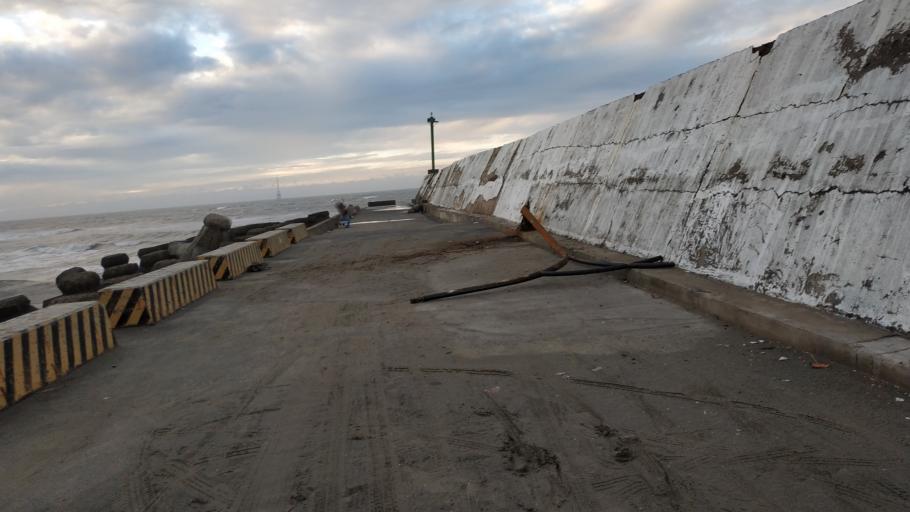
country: TW
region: Taiwan
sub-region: Miaoli
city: Miaoli
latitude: 24.7017
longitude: 120.8548
